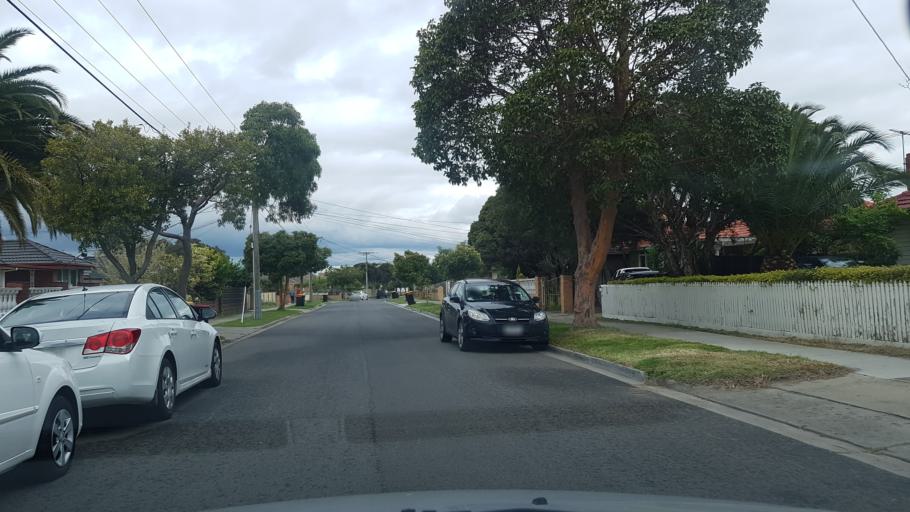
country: AU
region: Victoria
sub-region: Greater Dandenong
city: Springvale
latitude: -37.9372
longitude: 145.1489
